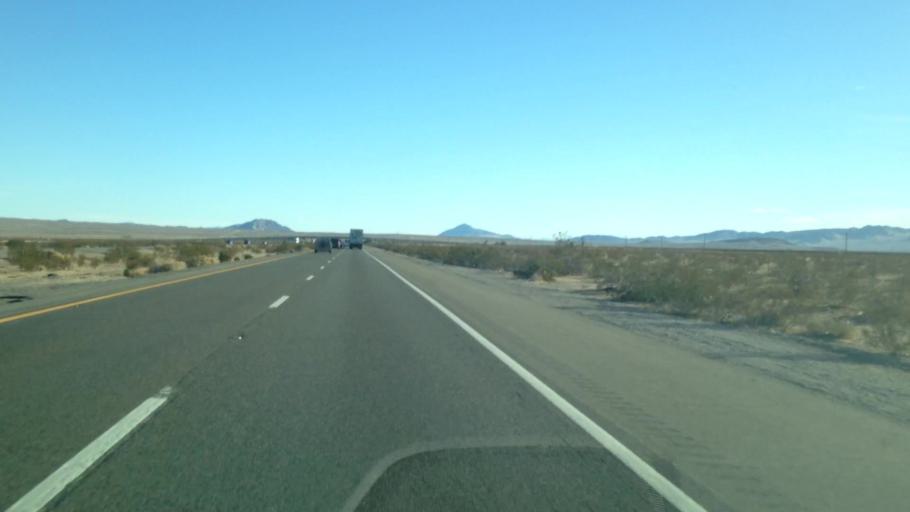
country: US
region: California
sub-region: San Bernardino County
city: Fort Irwin
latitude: 34.9800
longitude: -116.6071
